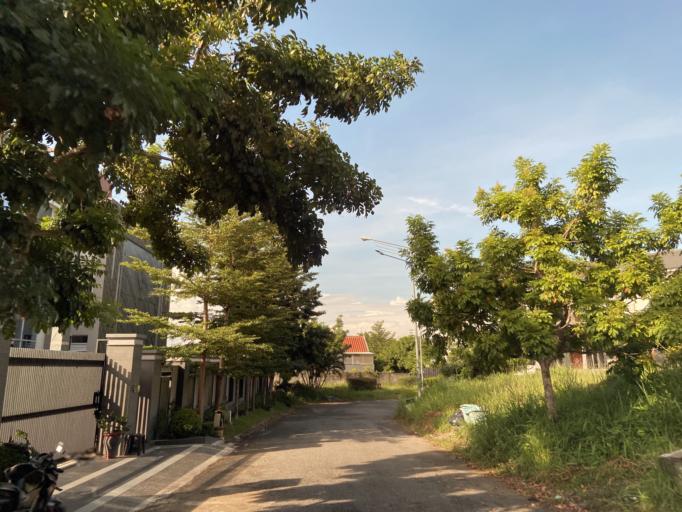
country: SG
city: Singapore
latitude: 1.0975
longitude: 104.0287
